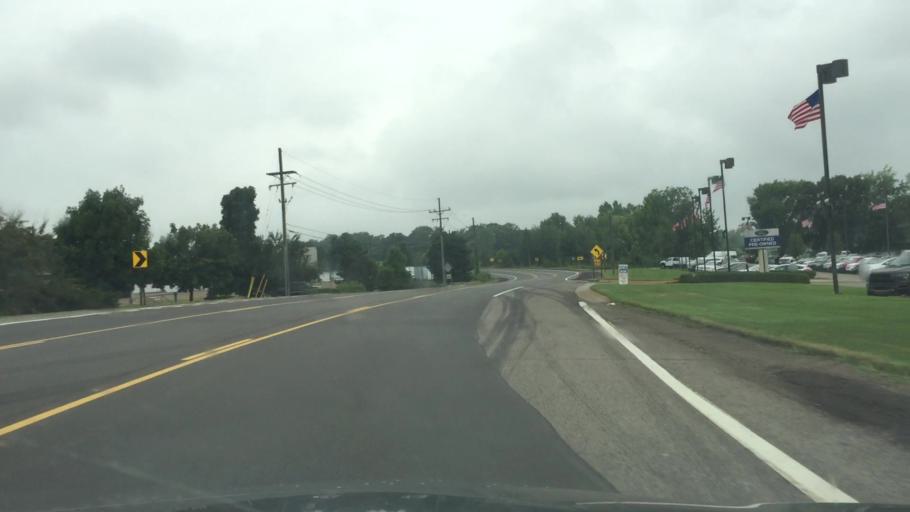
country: US
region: Michigan
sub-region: Oakland County
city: South Lyon
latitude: 42.5205
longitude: -83.6117
